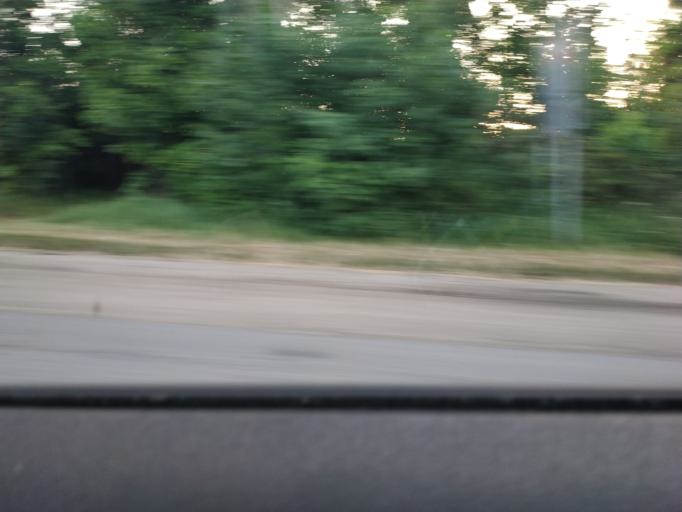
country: RU
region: Moskovskaya
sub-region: Shchelkovskiy Rayon
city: Grebnevo
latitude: 55.9677
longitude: 38.0838
